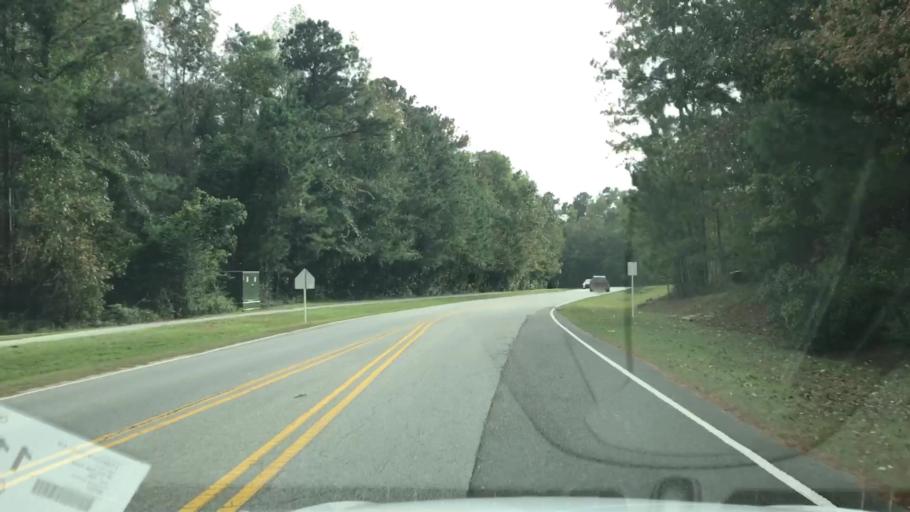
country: US
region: South Carolina
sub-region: Berkeley County
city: Sangaree
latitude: 33.0265
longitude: -80.1098
